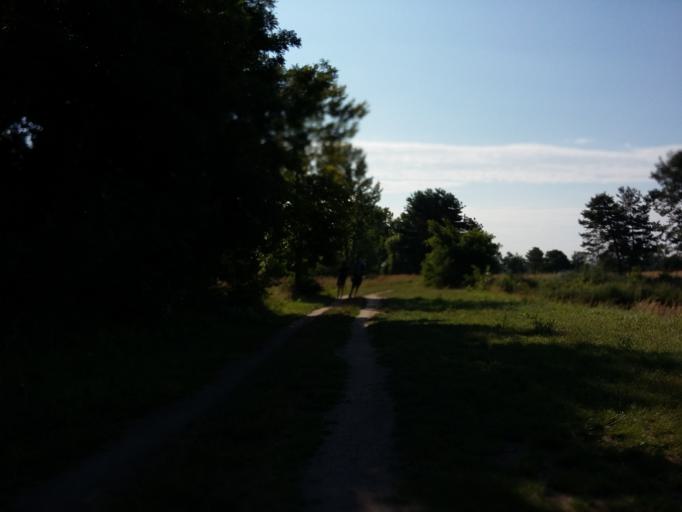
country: AT
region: Lower Austria
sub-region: Politischer Bezirk Ganserndorf
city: Drosing
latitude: 48.4946
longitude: 16.9605
